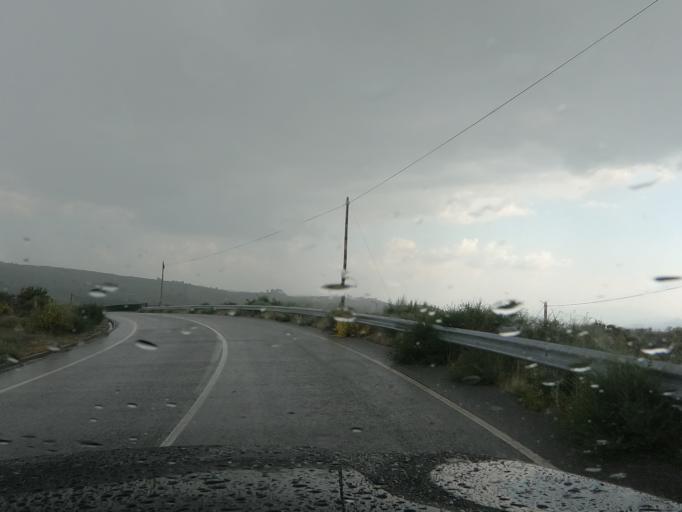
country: PT
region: Vila Real
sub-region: Vila Real
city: Vila Real
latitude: 41.3640
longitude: -7.6977
